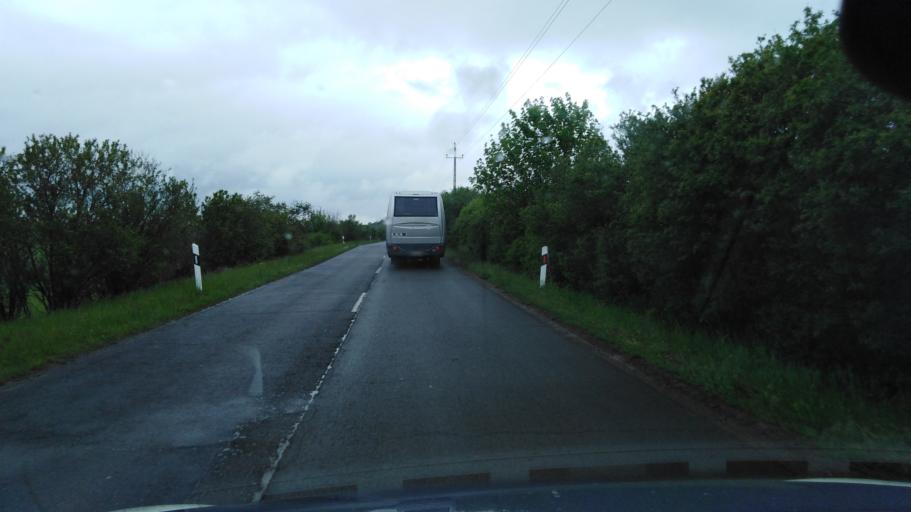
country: HU
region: Nograd
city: Rimoc
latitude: 48.0006
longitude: 19.6182
